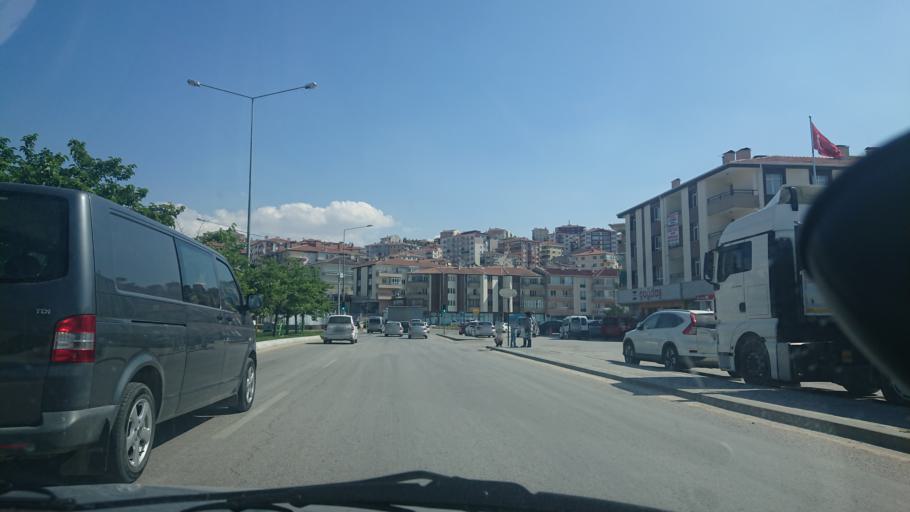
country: TR
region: Ankara
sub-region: Goelbasi
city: Golbasi
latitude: 39.8006
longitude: 32.8113
